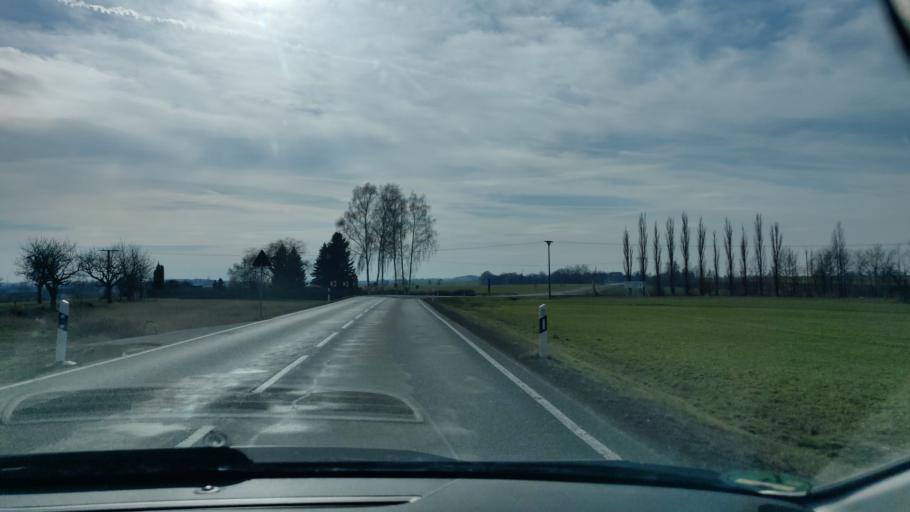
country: DE
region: Saxony
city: Wechselburg
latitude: 51.0235
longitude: 12.7480
